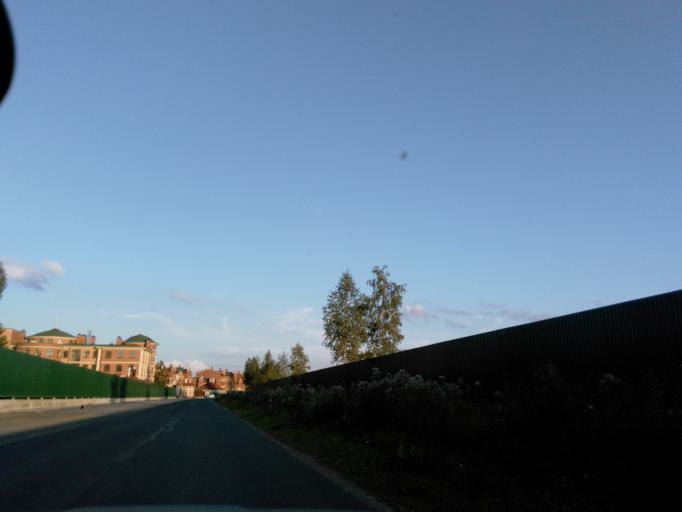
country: RU
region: Tverskaya
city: Konakovo
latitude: 56.6779
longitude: 36.7094
